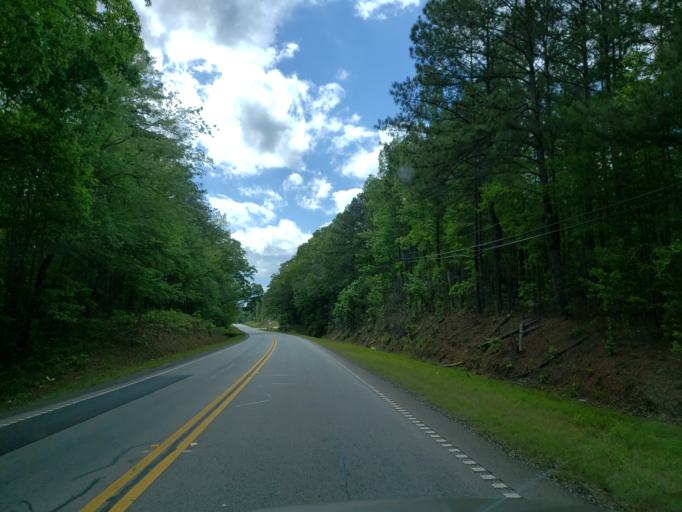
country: US
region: Georgia
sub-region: Haralson County
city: Tallapoosa
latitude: 33.7381
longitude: -85.2595
